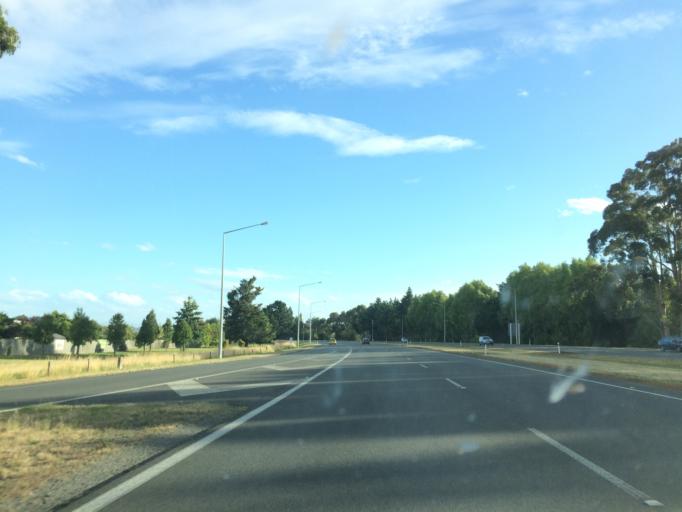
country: NZ
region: Canterbury
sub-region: Waimakariri District
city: Kaiapoi
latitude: -43.3887
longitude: 172.6404
